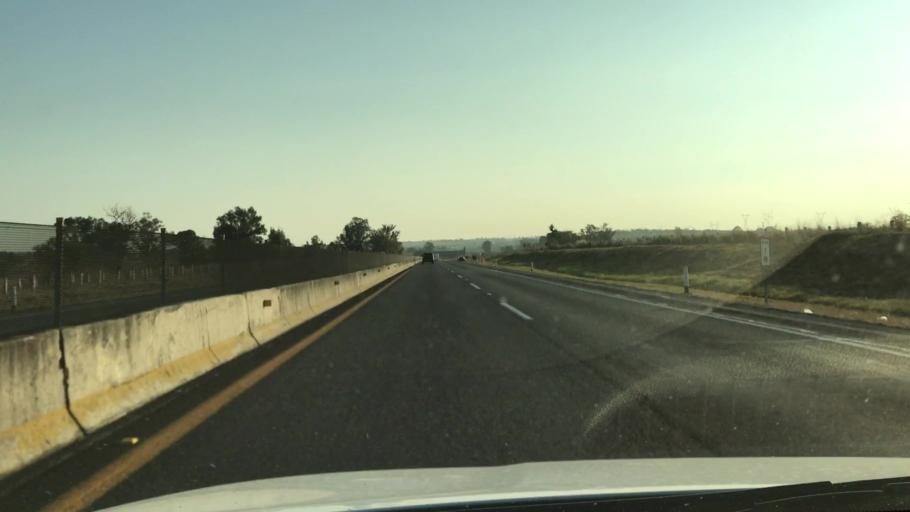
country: MX
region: Jalisco
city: Acatic
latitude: 20.7063
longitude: -102.9683
